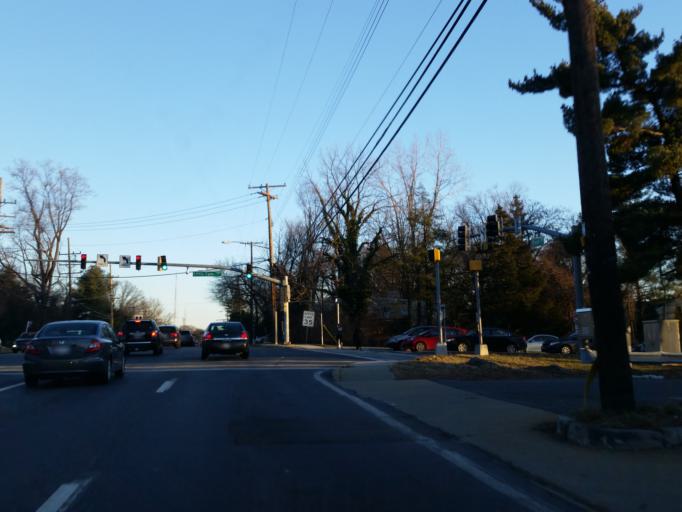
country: US
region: Maryland
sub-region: Montgomery County
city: Somerset
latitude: 38.9631
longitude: -77.1013
